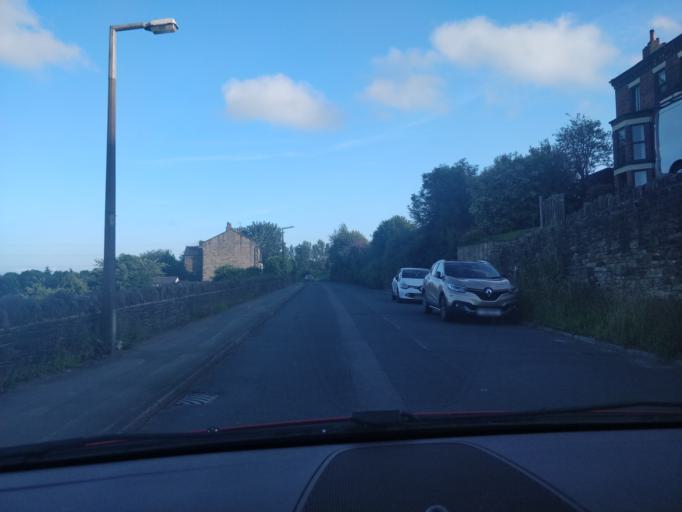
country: GB
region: England
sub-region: Lancashire
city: Appley Bridge
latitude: 53.5374
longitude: -2.7213
